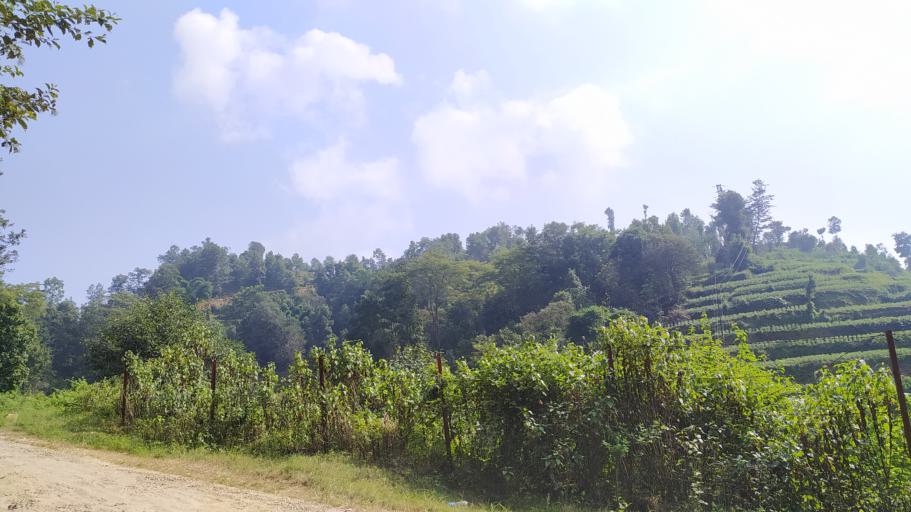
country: NP
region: Central Region
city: Panaoti
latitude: 27.5867
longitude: 85.5208
